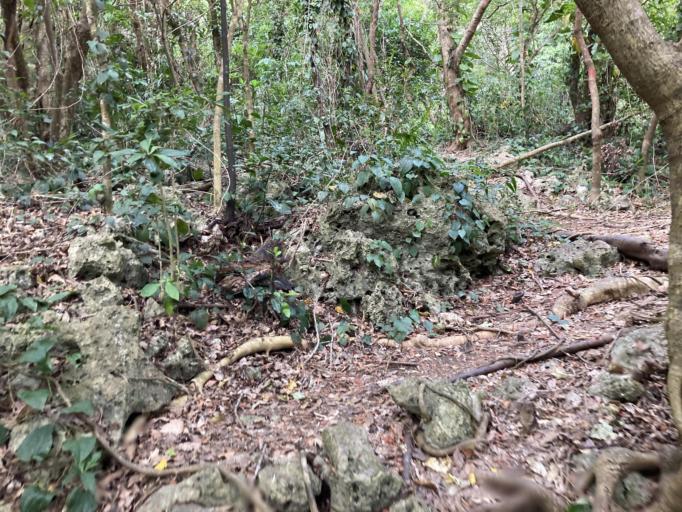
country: JP
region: Okinawa
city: Tomigusuku
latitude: 26.1423
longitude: 127.7833
